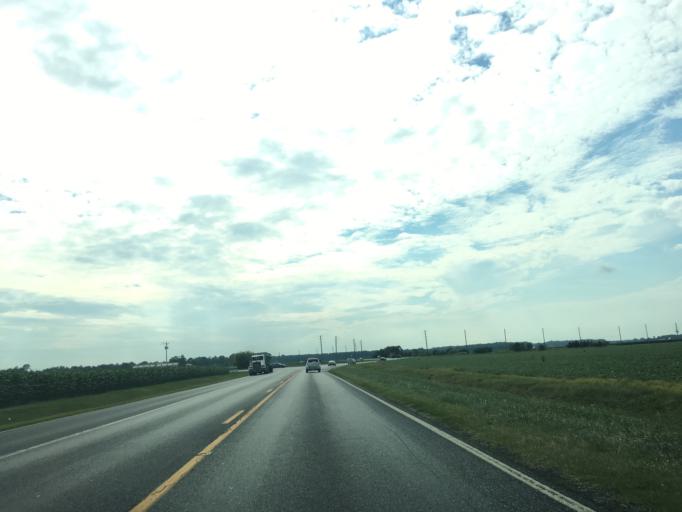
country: US
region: Delaware
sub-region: Sussex County
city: Bridgeville
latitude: 38.7621
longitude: -75.6071
